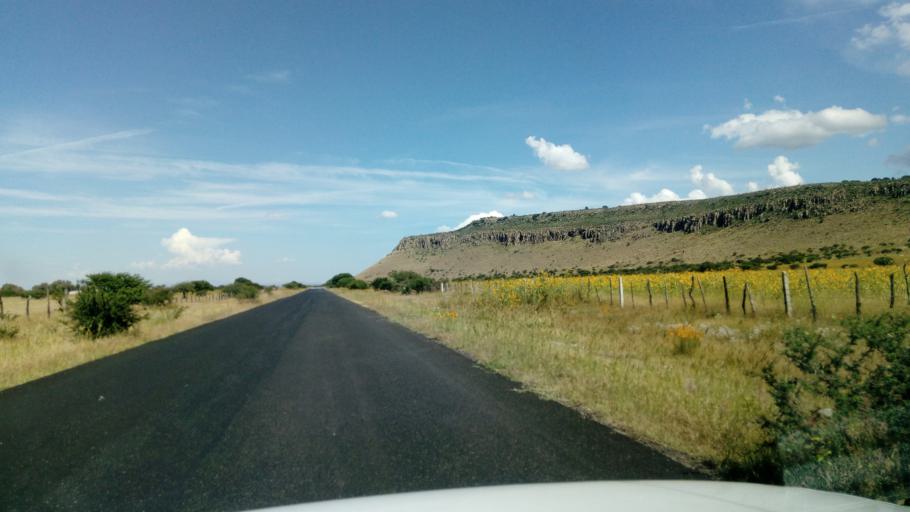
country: MX
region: Durango
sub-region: Durango
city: Jose Refugio Salcido
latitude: 23.8155
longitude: -104.4836
